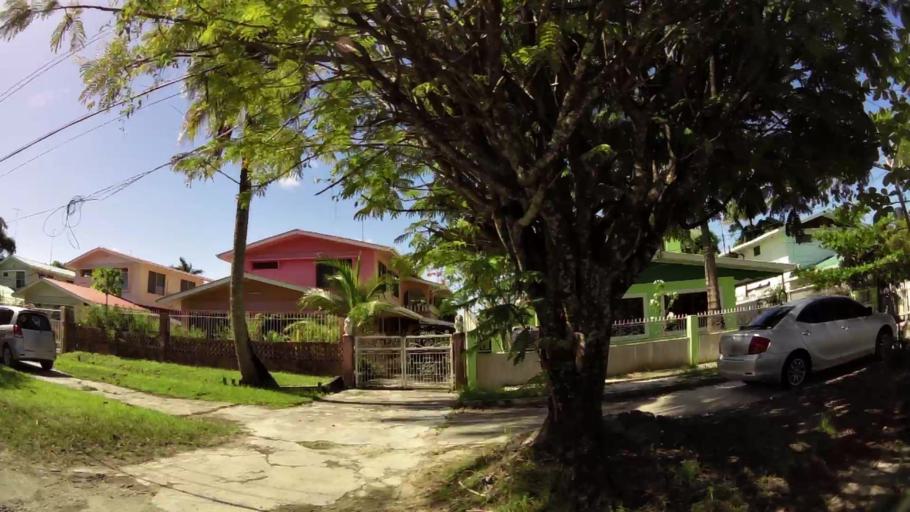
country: GY
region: Demerara-Mahaica
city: Georgetown
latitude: 6.8084
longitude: -58.1391
